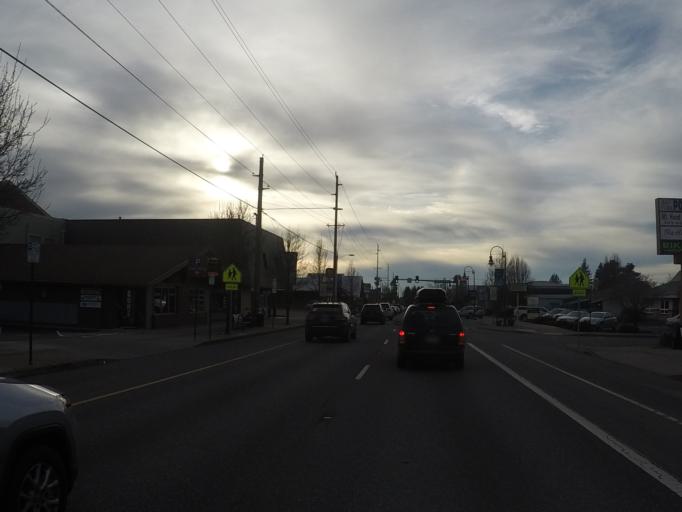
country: US
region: Oregon
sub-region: Clackamas County
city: Sandy
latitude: 45.3973
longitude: -122.2603
